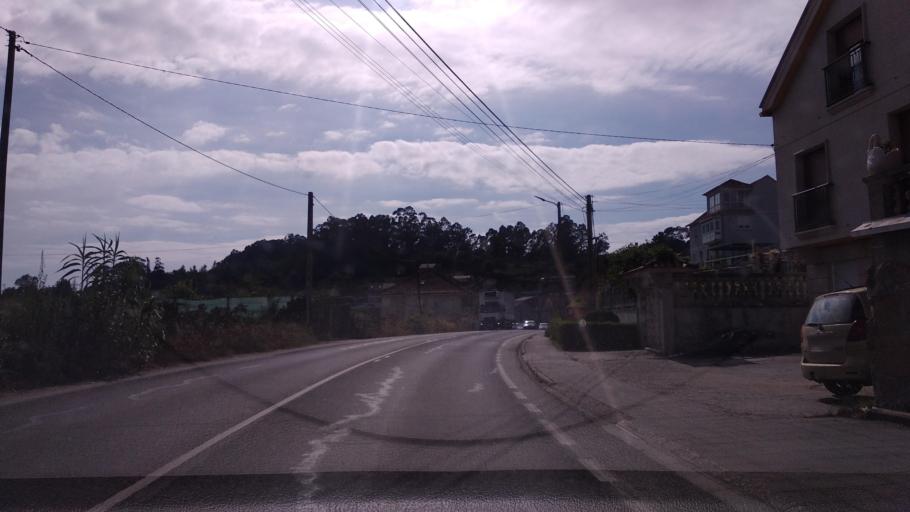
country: ES
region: Galicia
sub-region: Provincia de Pontevedra
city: Moana
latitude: 42.2759
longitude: -8.7489
